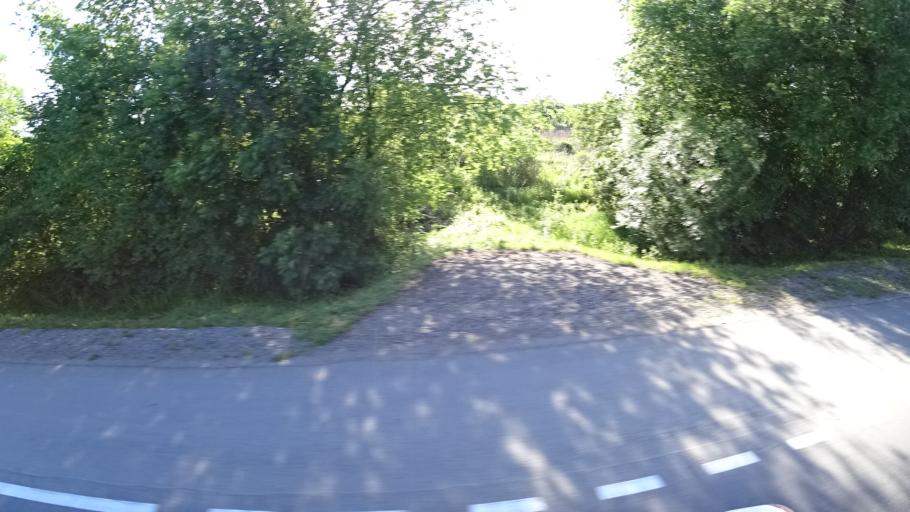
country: RU
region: Khabarovsk Krai
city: Khor
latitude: 47.8553
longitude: 134.9619
